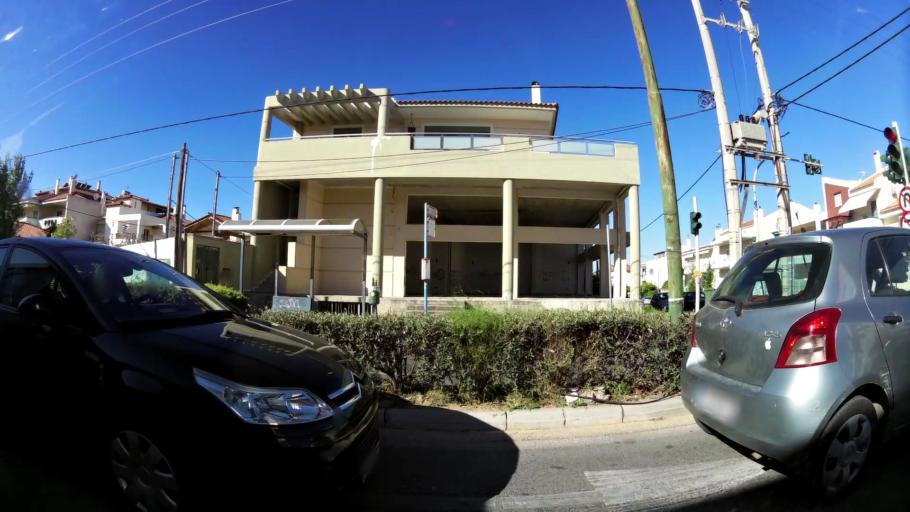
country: GR
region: Attica
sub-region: Nomarchia Anatolikis Attikis
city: Gerakas
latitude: 38.0161
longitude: 23.8603
